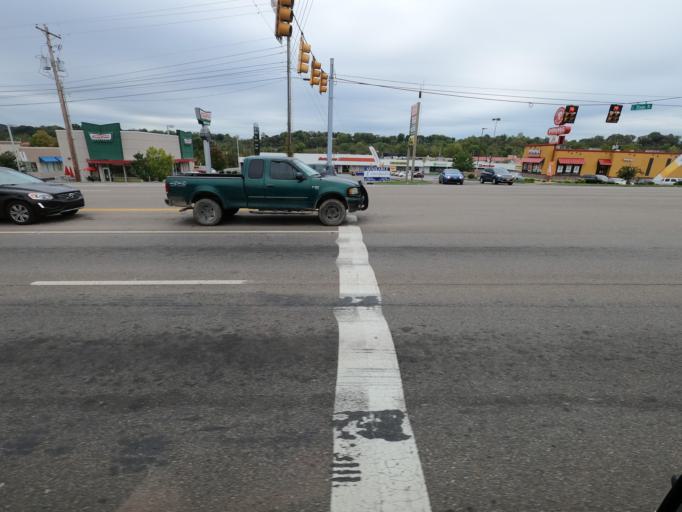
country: US
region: Tennessee
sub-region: Sullivan County
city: Kingsport
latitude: 36.5481
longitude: -82.5192
